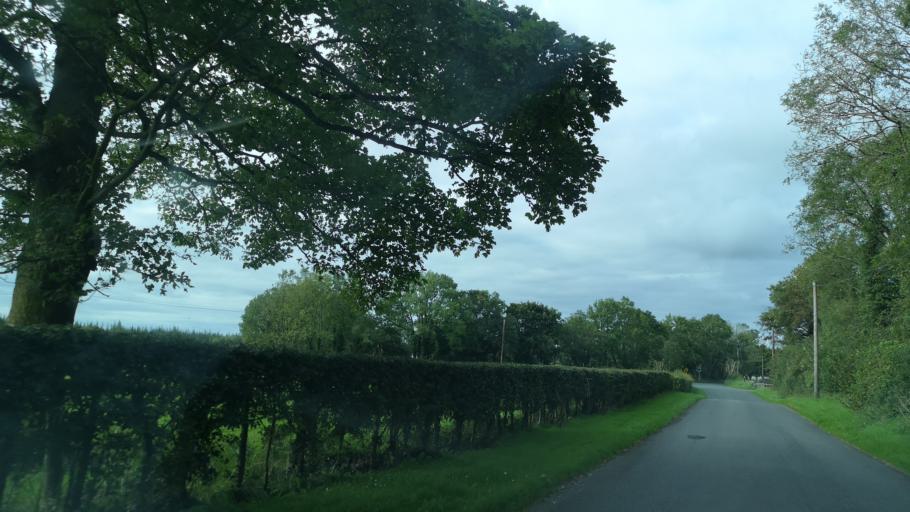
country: IE
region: Connaught
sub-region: County Galway
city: Ballinasloe
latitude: 53.3232
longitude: -8.1027
